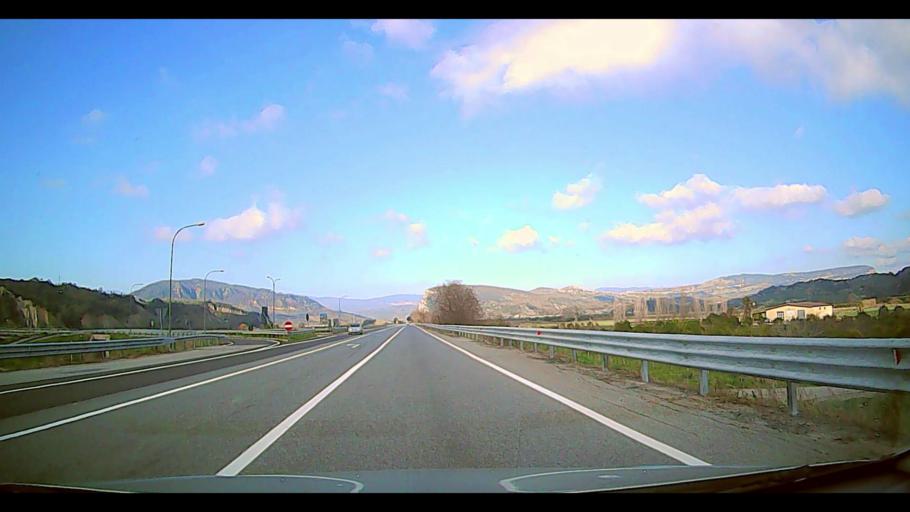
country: IT
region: Calabria
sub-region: Provincia di Crotone
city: Santa Severina
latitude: 39.1752
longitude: 16.9338
